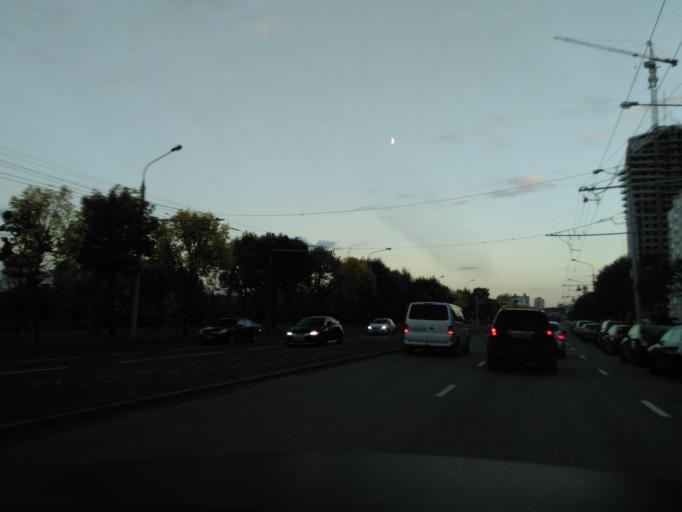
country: BY
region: Minsk
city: Minsk
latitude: 53.9260
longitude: 27.6392
